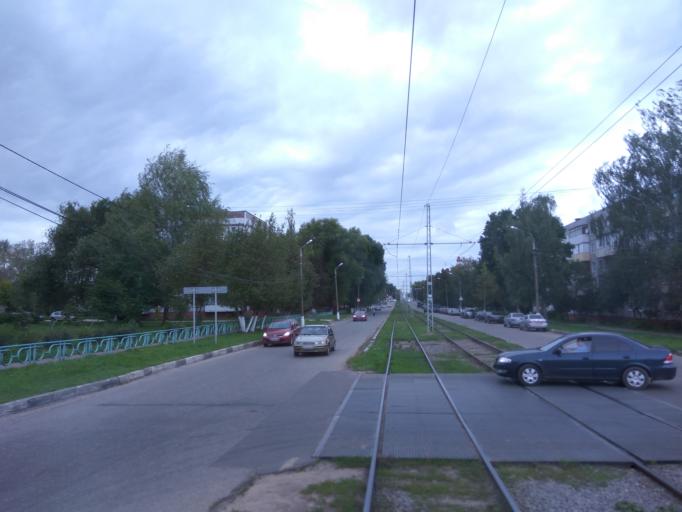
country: RU
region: Moskovskaya
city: Kolomna
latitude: 55.0790
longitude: 38.7685
